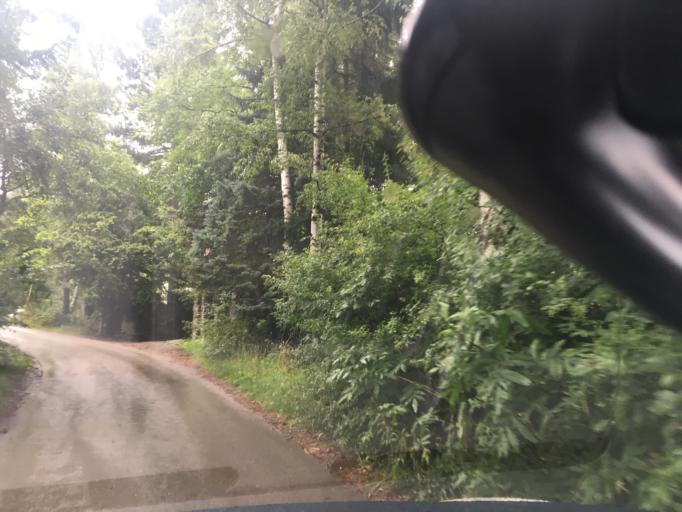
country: BG
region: Sofia-Capital
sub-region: Stolichna Obshtina
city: Sofia
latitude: 42.5851
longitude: 23.3454
